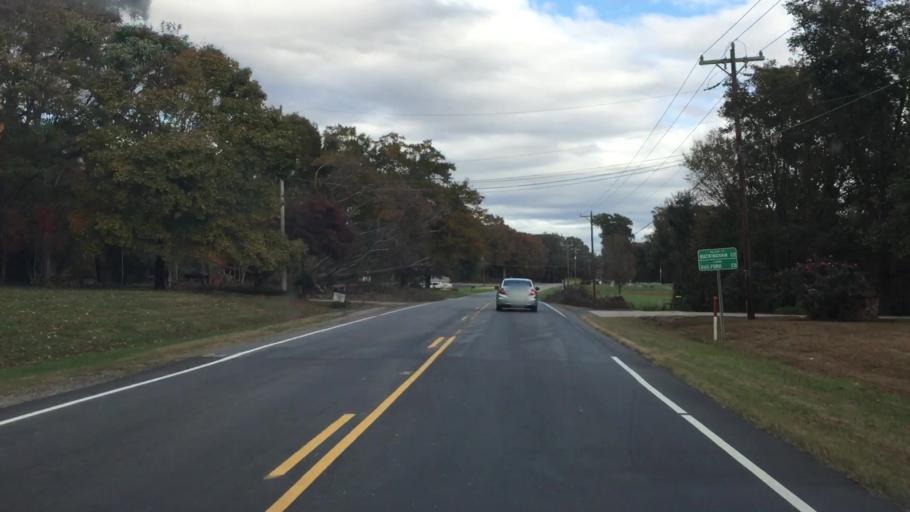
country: US
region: North Carolina
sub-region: Guilford County
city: Summerfield
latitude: 36.2532
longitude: -79.8953
